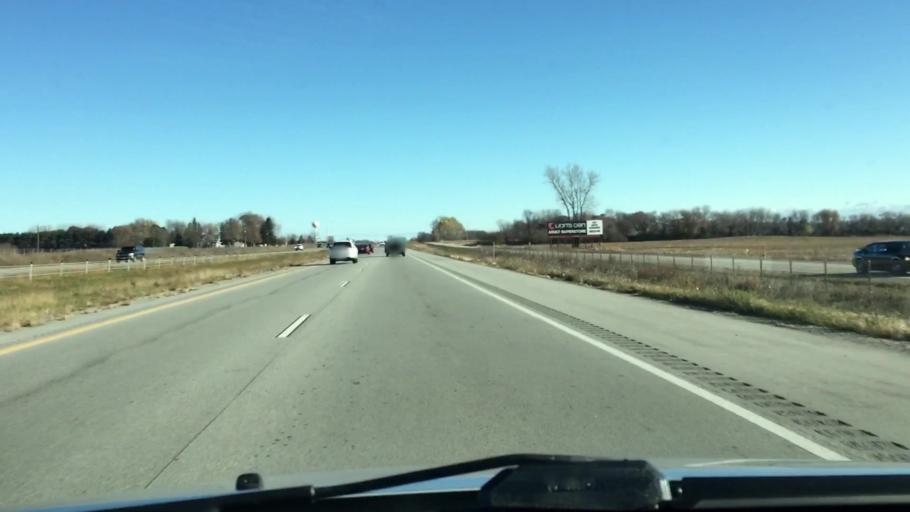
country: US
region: Wisconsin
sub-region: Brown County
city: Wrightstown
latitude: 44.4025
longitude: -88.1476
